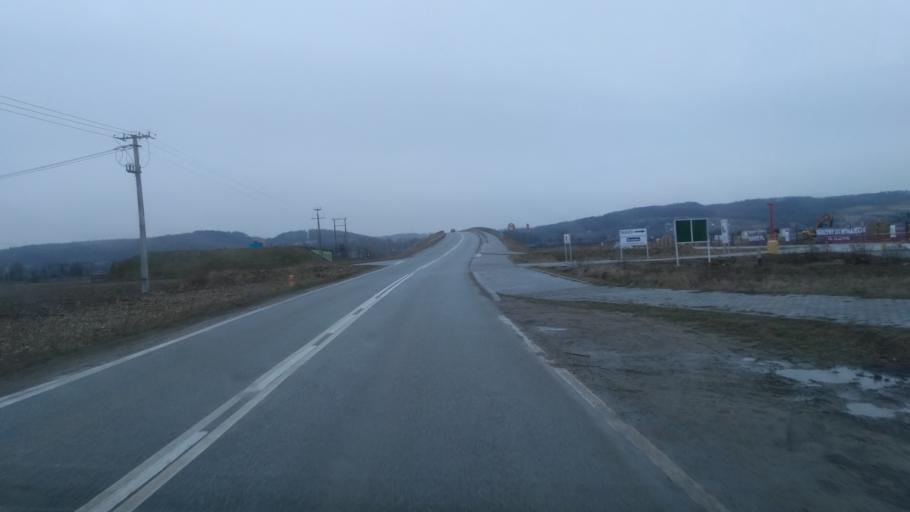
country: PL
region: Subcarpathian Voivodeship
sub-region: Powiat debicki
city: Brzeznica
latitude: 50.0686
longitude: 21.4727
